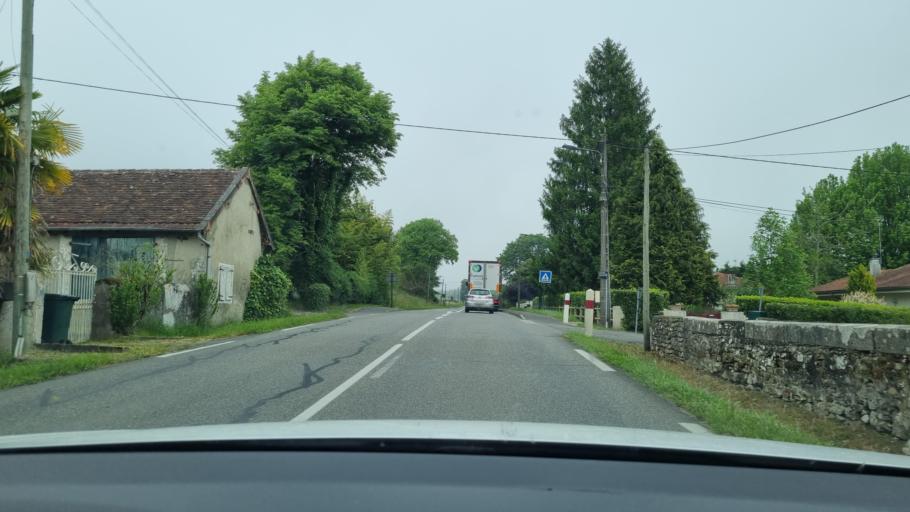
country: FR
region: Aquitaine
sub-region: Departement des Pyrenees-Atlantiques
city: Orthez
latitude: 43.5036
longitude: -0.7429
